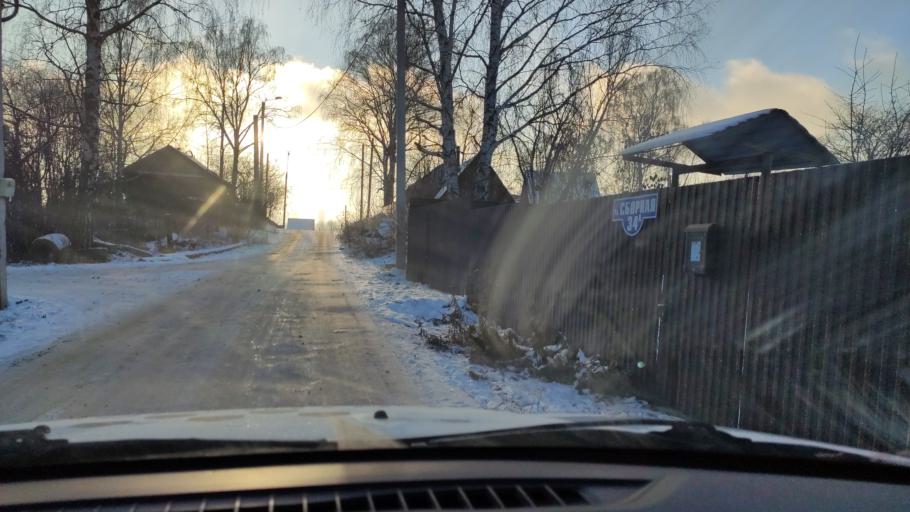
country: RU
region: Perm
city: Perm
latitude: 58.0308
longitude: 56.2292
